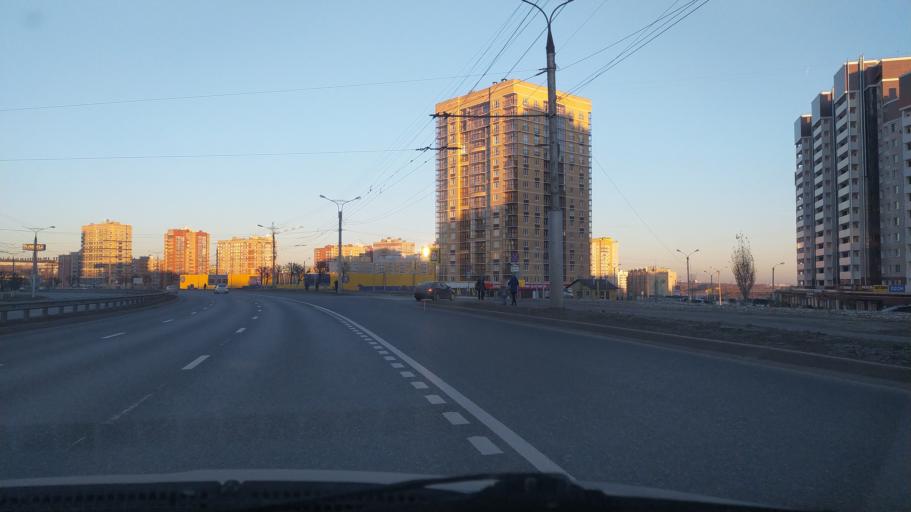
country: RU
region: Chuvashia
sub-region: Cheboksarskiy Rayon
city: Cheboksary
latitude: 56.1068
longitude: 47.3254
